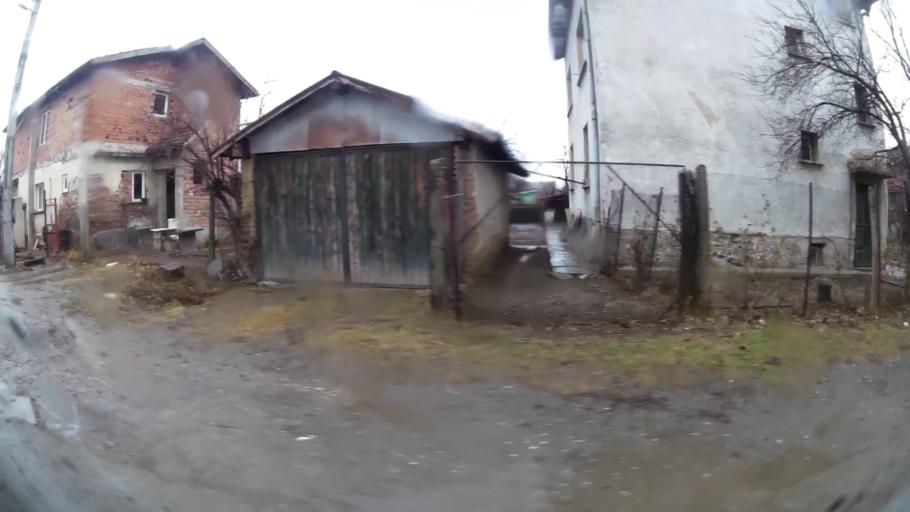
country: BG
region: Sofia-Capital
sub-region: Stolichna Obshtina
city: Sofia
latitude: 42.6569
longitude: 23.4289
